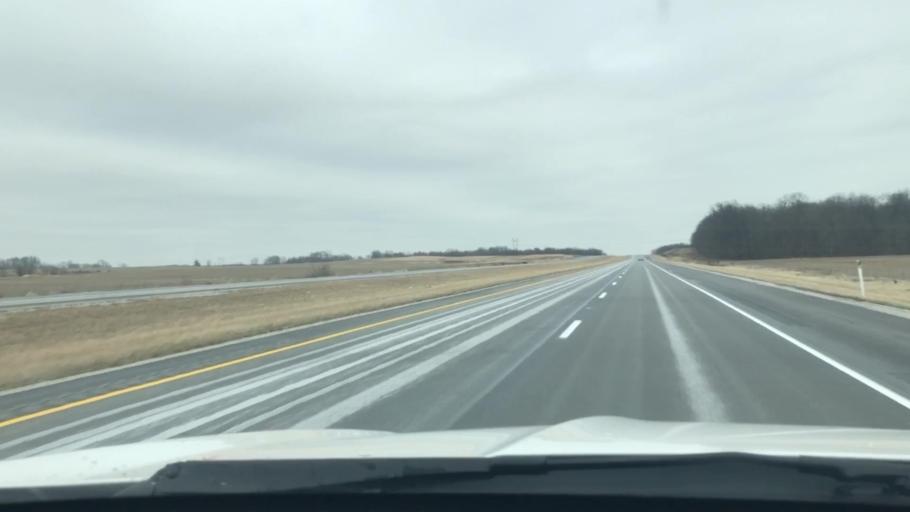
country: US
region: Indiana
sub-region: Cass County
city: Walton
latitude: 40.7534
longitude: -86.2036
